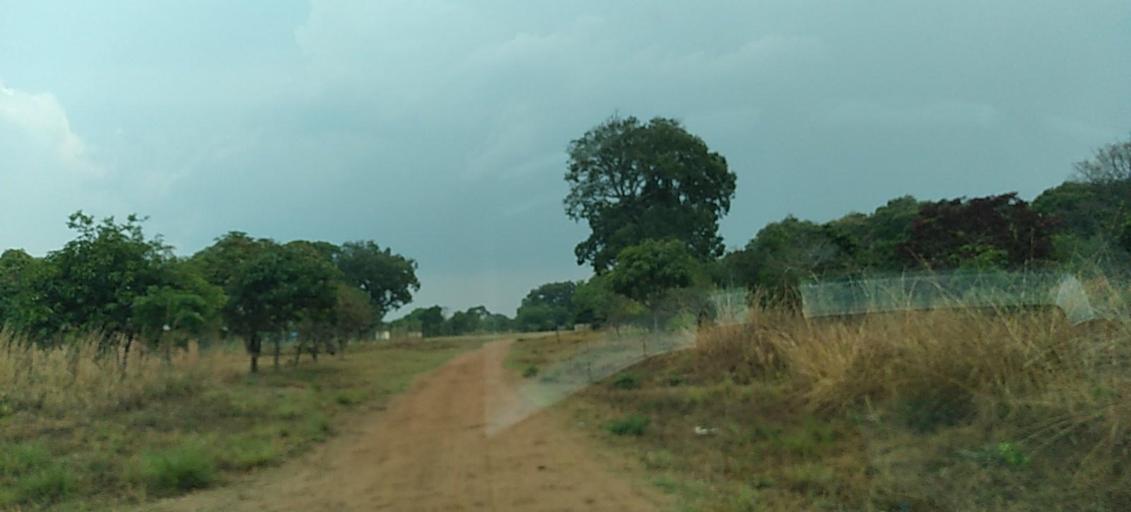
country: ZM
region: North-Western
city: Mwinilunga
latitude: -11.4495
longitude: 24.5906
